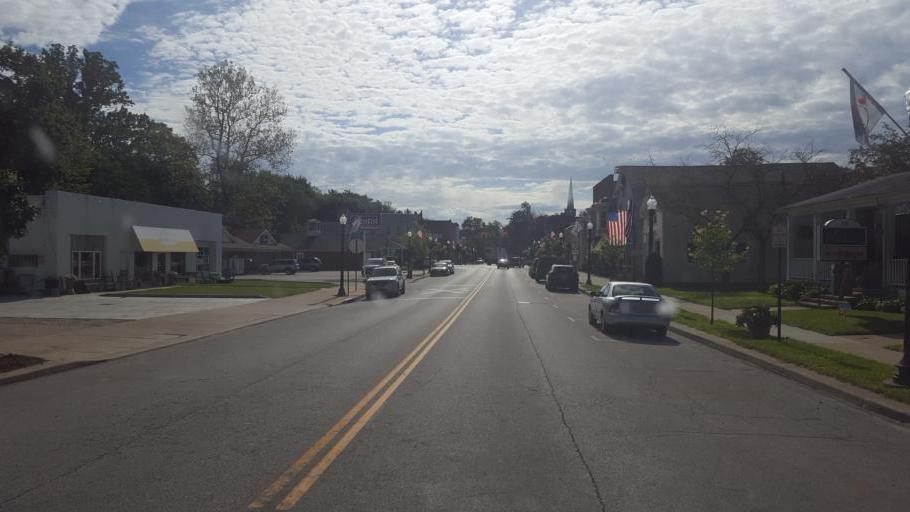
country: US
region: Ohio
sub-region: Medina County
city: Seville
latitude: 41.0101
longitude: -81.8637
